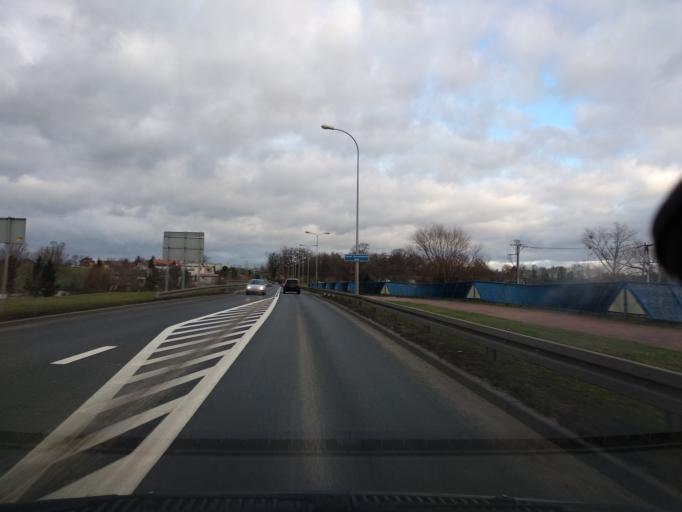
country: PL
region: Greater Poland Voivodeship
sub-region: Kalisz
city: Kalisz
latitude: 51.7724
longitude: 18.0736
